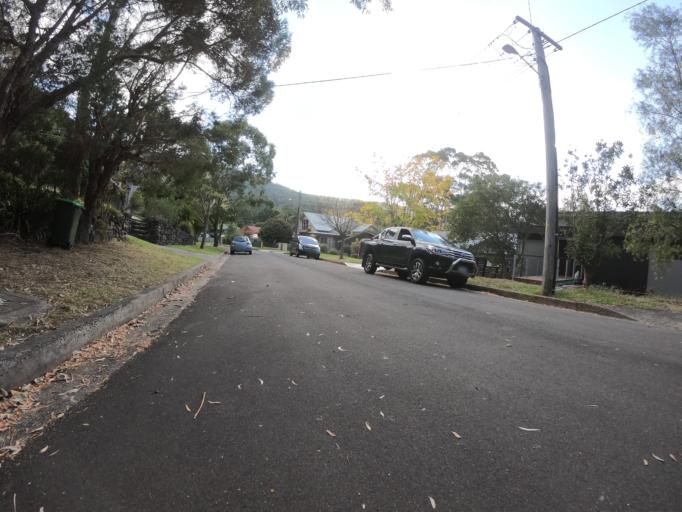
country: AU
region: New South Wales
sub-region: Wollongong
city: Cordeaux Heights
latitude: -34.4339
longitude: 150.8140
